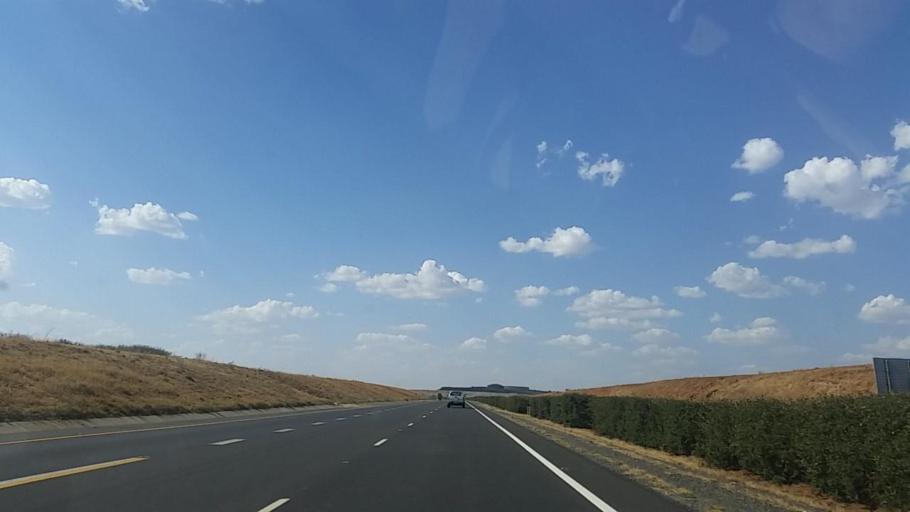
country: ZA
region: Orange Free State
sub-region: Mangaung Metropolitan Municipality
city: Bloemfontein
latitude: -29.1978
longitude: 26.1918
